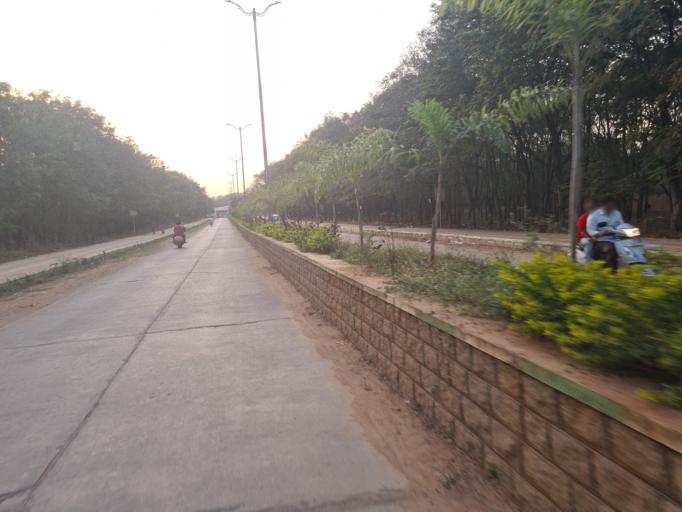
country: IN
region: Telangana
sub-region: Medak
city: Serilingampalle
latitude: 17.4780
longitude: 78.2939
